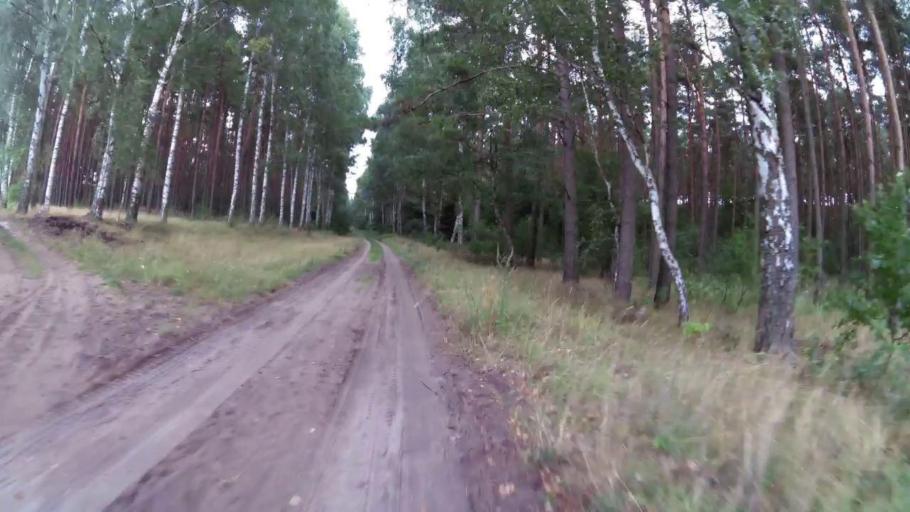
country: PL
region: West Pomeranian Voivodeship
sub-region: Powiat mysliborski
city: Debno
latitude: 52.7826
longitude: 14.7150
